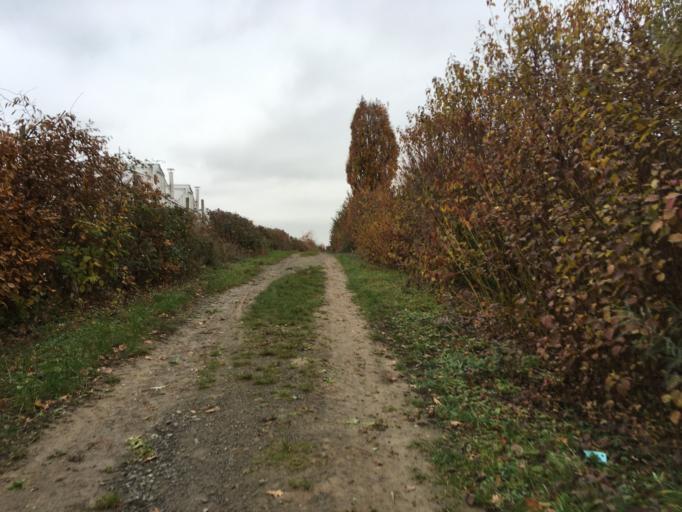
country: DE
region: Baden-Wuerttemberg
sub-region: Regierungsbezirk Stuttgart
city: Heilbronn
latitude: 49.1551
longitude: 9.1854
